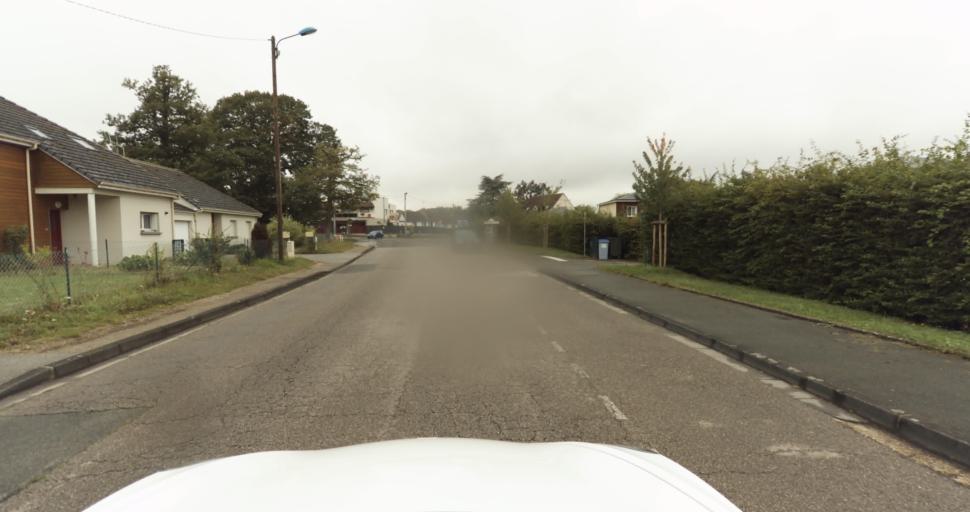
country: FR
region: Haute-Normandie
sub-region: Departement de l'Eure
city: Evreux
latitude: 49.0342
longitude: 1.1342
